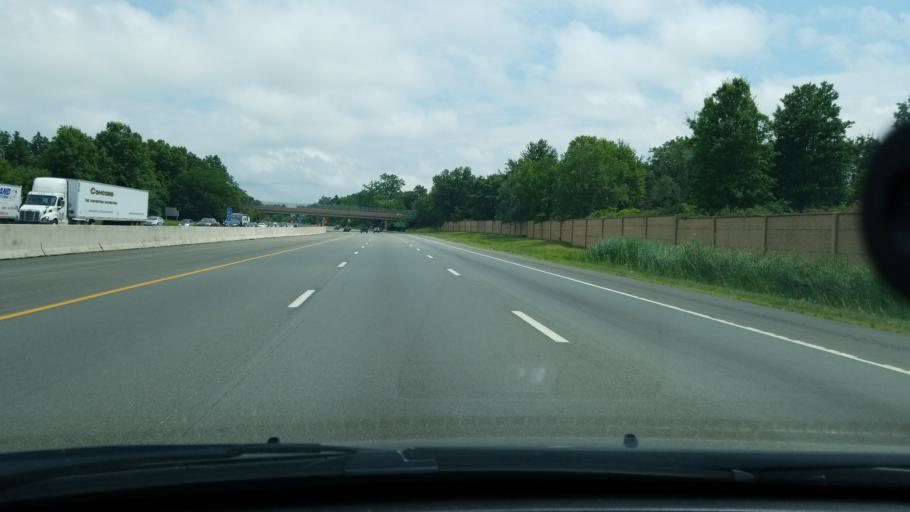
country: US
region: Ohio
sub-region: Cuyahoga County
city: Westlake
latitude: 41.4671
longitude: -81.9339
